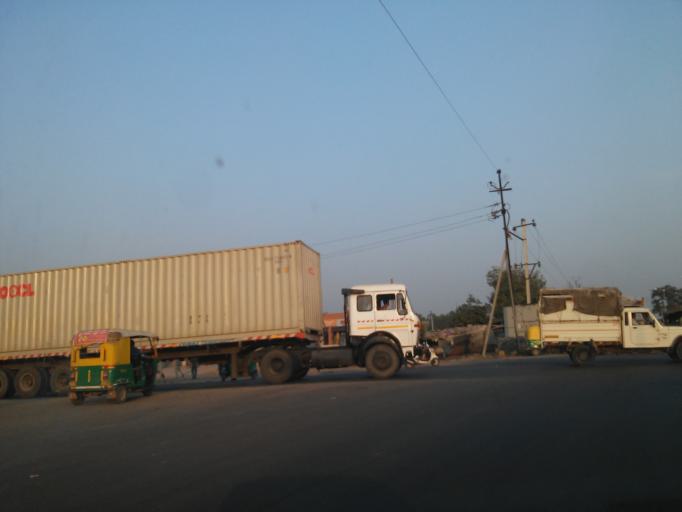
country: IN
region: Gujarat
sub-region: Ahmadabad
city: Sarkhej
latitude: 22.9879
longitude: 72.4713
